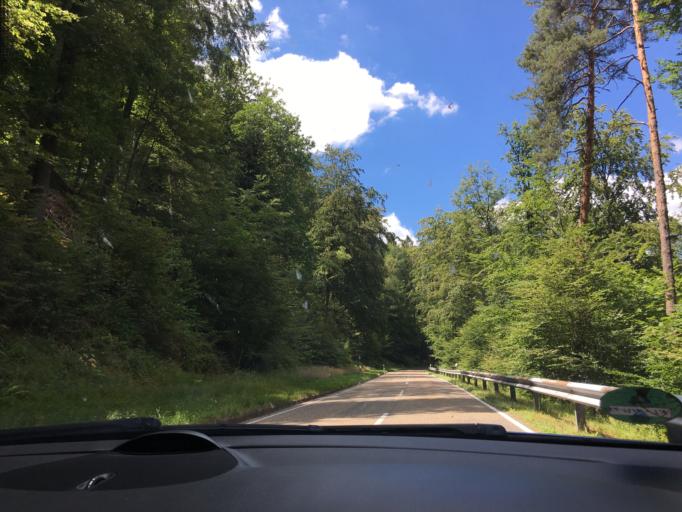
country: DE
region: Rheinland-Pfalz
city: Hauenstein
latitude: 49.2076
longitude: 7.8426
